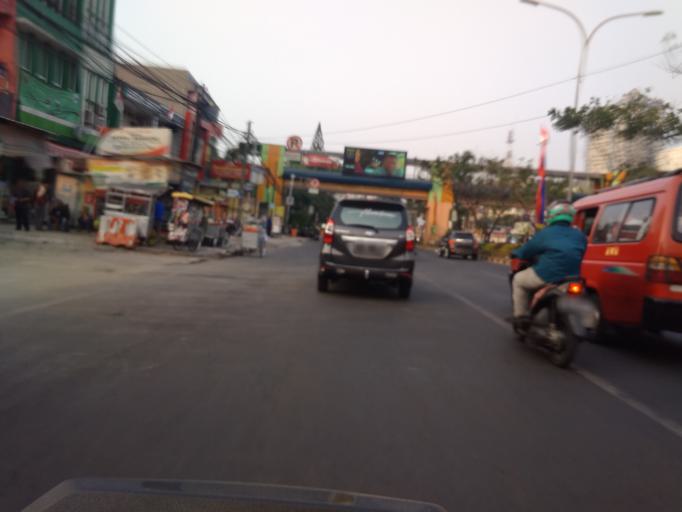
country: ID
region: West Java
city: Depok
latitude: -6.3954
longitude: 106.8221
